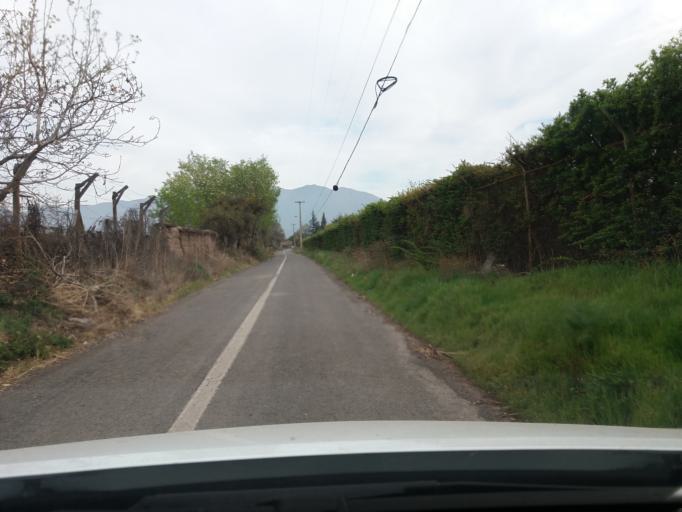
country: CL
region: Valparaiso
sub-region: Provincia de Los Andes
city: Los Andes
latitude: -32.8243
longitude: -70.6438
